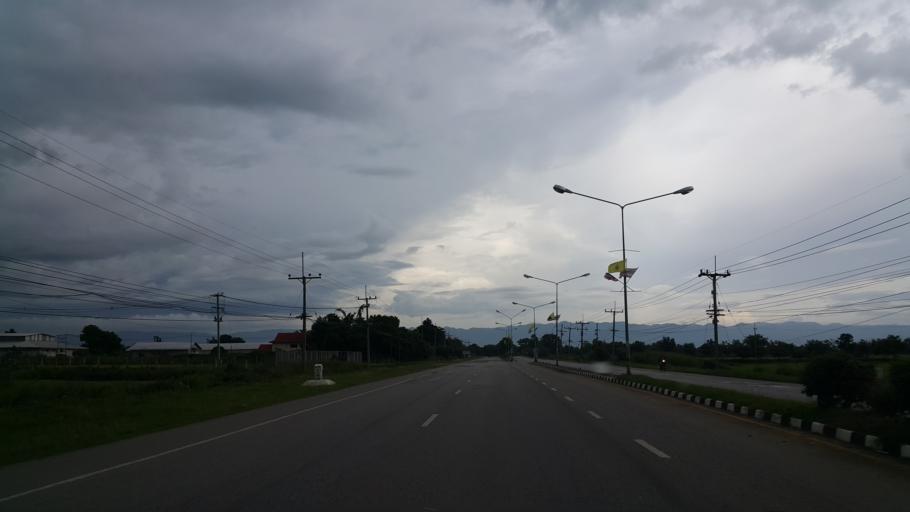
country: TH
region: Phayao
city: Dok Kham Tai
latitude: 19.1557
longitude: 99.9535
